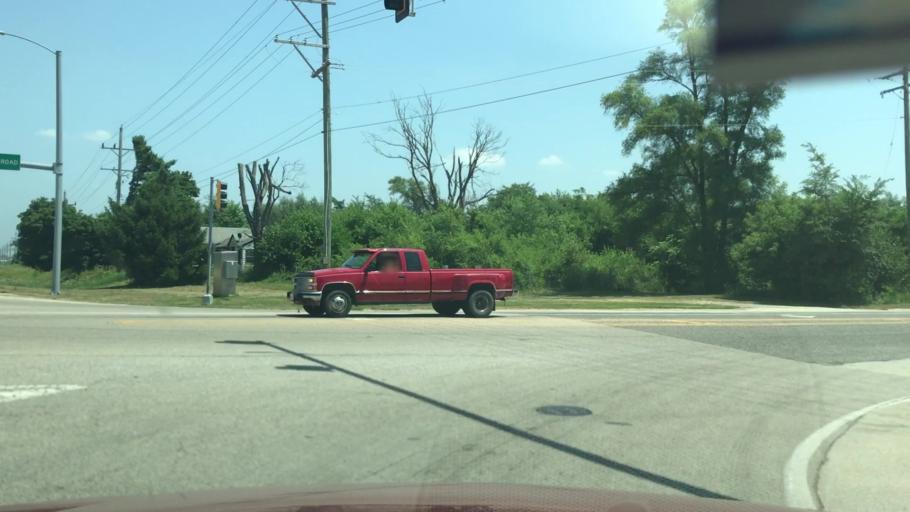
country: US
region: Illinois
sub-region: Winnebago County
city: Cherry Valley
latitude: 42.2398
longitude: -88.9008
